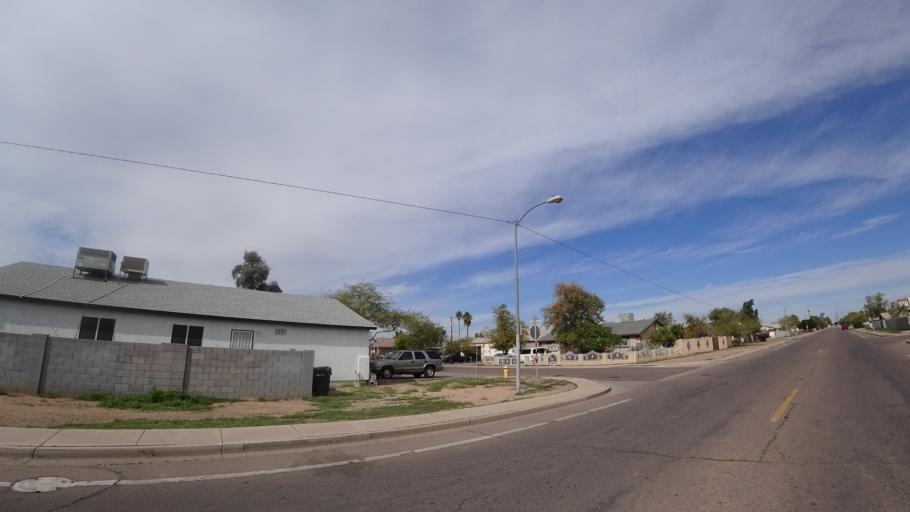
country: US
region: Arizona
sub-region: Maricopa County
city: Phoenix
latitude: 33.4672
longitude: -112.1258
